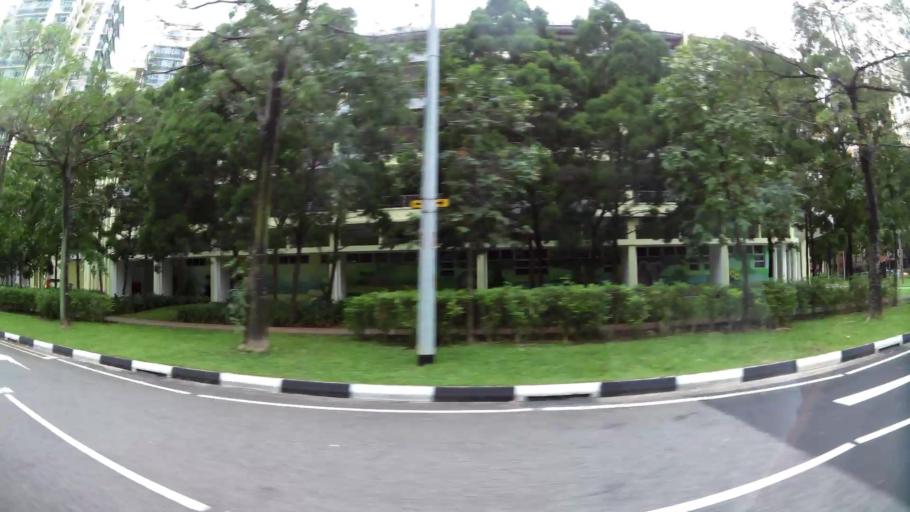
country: MY
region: Johor
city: Kampung Pasir Gudang Baru
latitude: 1.4025
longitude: 103.9063
